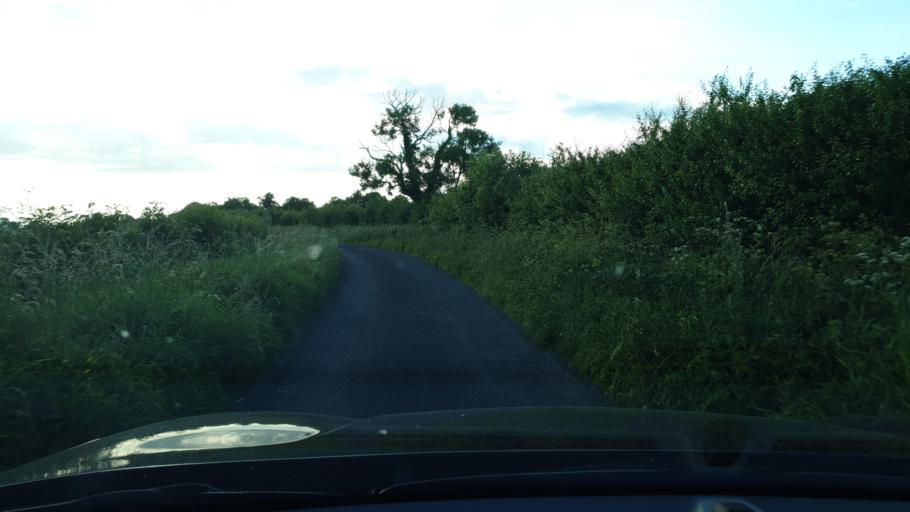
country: IE
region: Leinster
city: Hartstown
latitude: 53.4456
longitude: -6.3961
